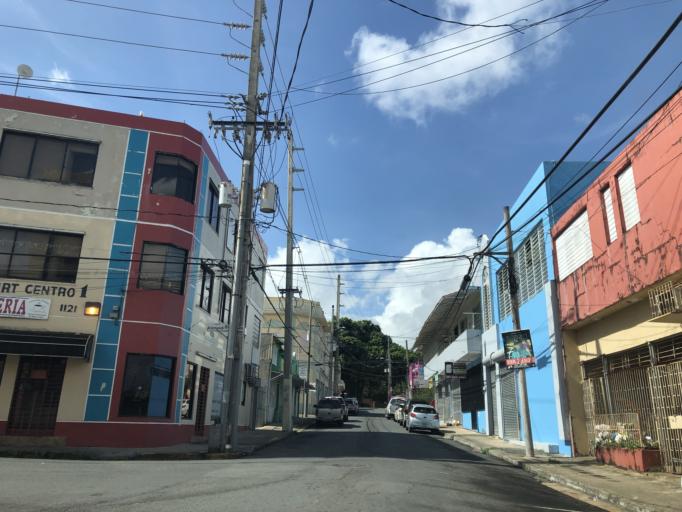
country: PR
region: Trujillo Alto
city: Trujillo Alto
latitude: 18.3970
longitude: -66.0476
